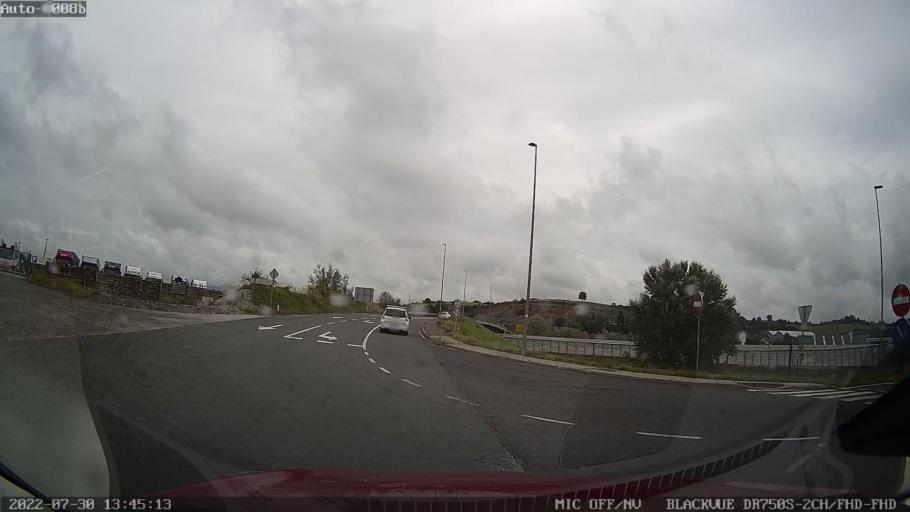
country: SI
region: Ivancna Gorica
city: Sentvid pri Sticni
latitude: 45.9226
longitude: 14.8891
